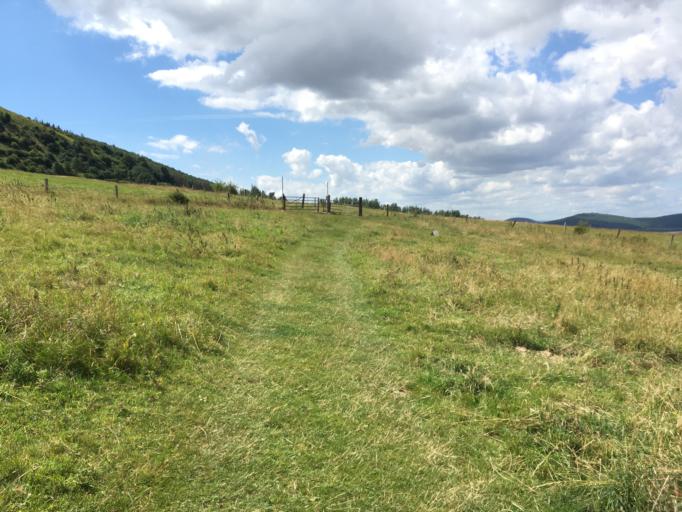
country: DE
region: Hesse
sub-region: Regierungsbezirk Kassel
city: Zierenberg
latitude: 51.3590
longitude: 9.3480
